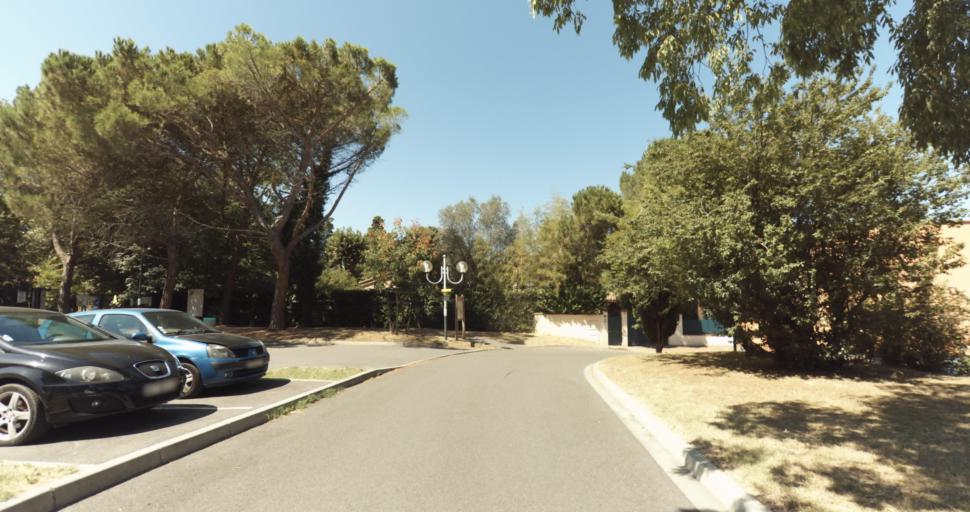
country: FR
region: Midi-Pyrenees
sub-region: Departement de la Haute-Garonne
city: L'Union
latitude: 43.6538
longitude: 1.4778
